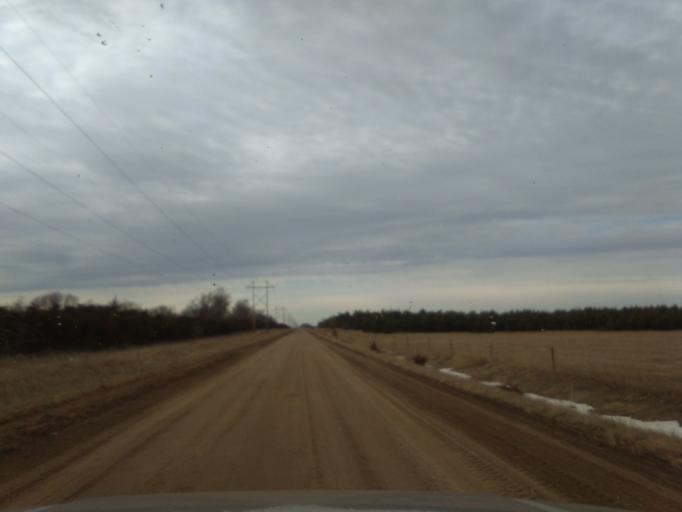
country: US
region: Nebraska
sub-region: Buffalo County
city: Gibbon
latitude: 40.6549
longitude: -98.7720
